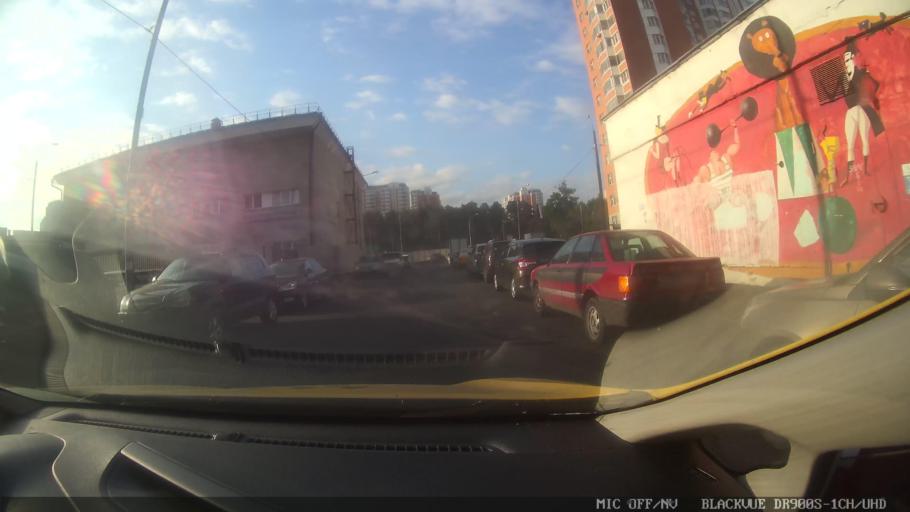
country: RU
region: Moscow
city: Nekrasovka
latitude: 55.6859
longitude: 37.9223
